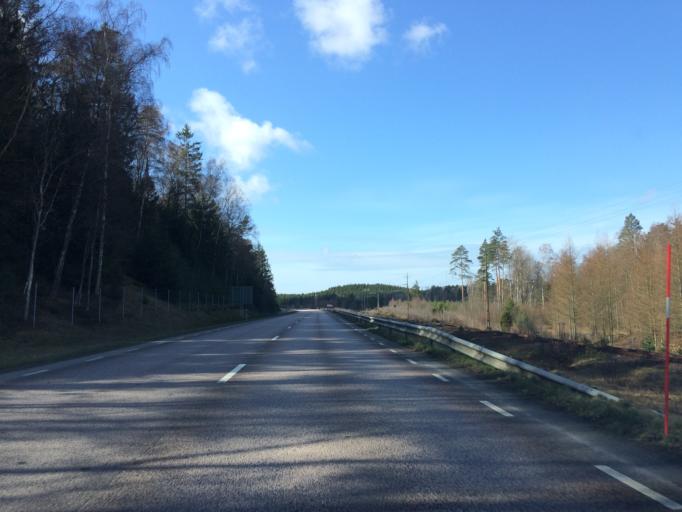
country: SE
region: Halland
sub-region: Laholms Kommun
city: Knared
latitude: 56.5203
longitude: 13.2756
